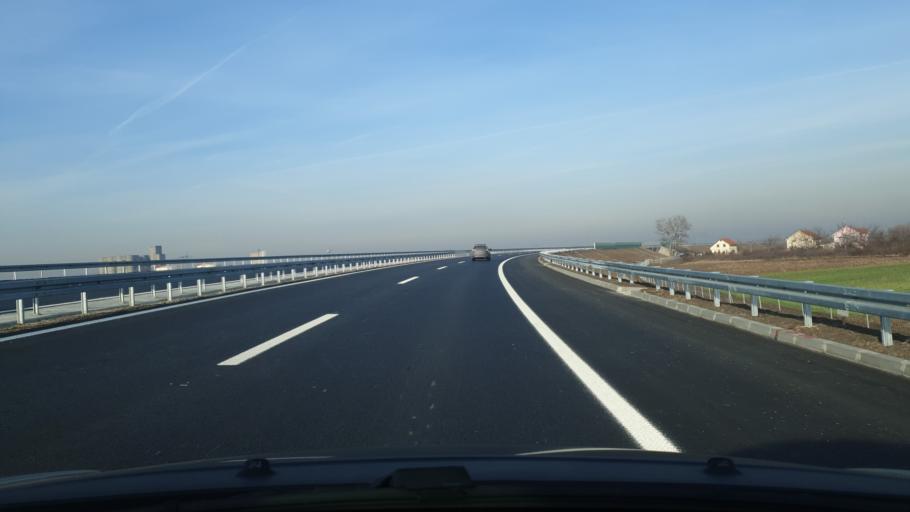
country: RS
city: Becmen
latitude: 44.7625
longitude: 20.2456
